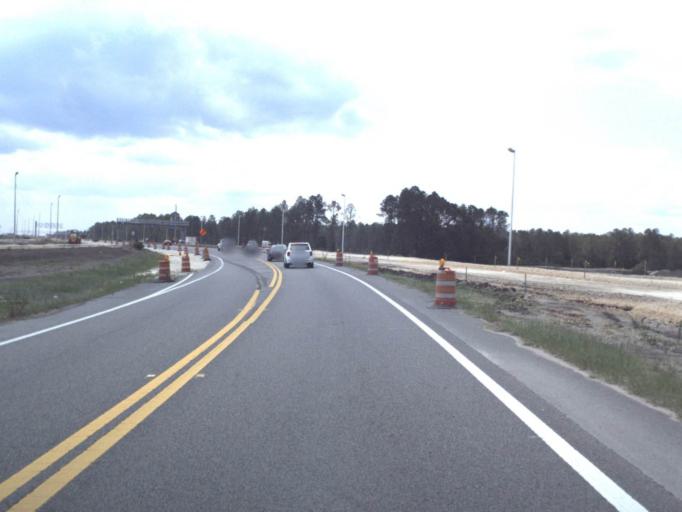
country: US
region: Florida
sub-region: Clay County
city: Bellair-Meadowbrook Terrace
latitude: 30.2498
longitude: -81.8472
